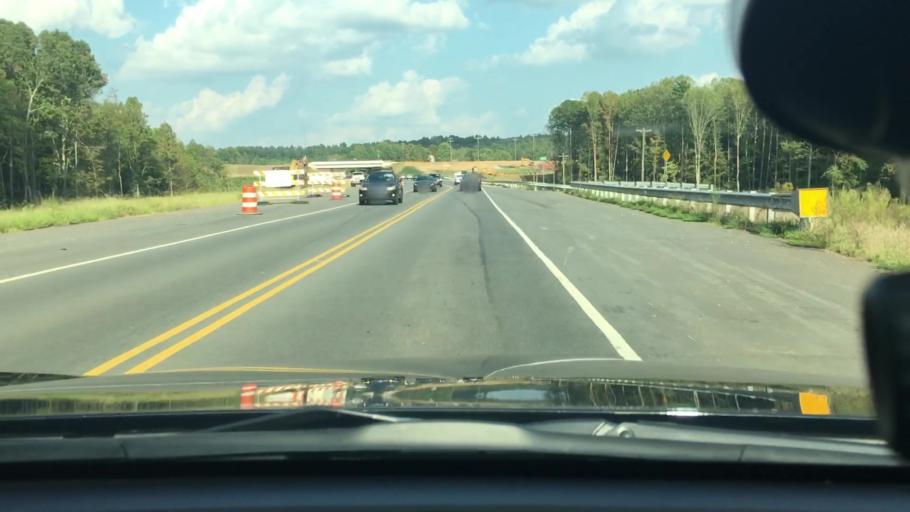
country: US
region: North Carolina
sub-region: Randolph County
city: Asheboro
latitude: 35.6734
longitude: -79.8677
